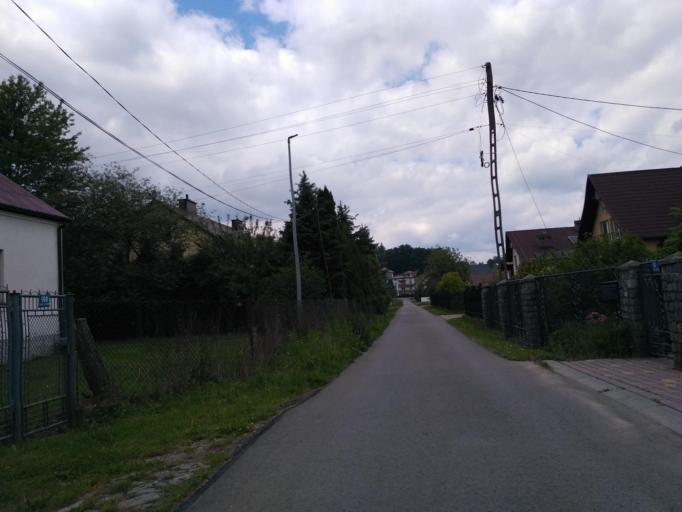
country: PL
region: Subcarpathian Voivodeship
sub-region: Powiat strzyzowski
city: Czudec
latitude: 49.9324
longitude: 21.8494
